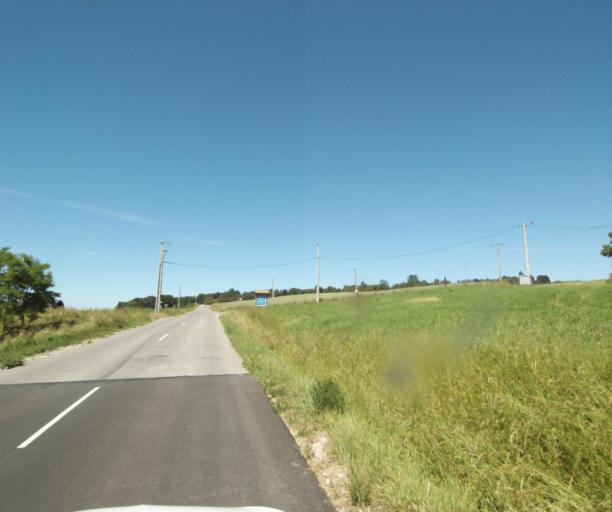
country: FR
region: Rhone-Alpes
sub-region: Departement de la Haute-Savoie
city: Ballaison
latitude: 46.2966
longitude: 6.3209
